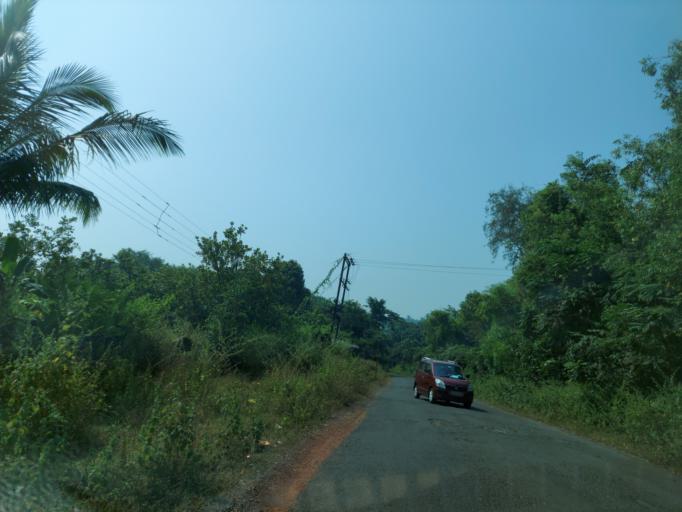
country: IN
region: Maharashtra
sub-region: Sindhudurg
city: Kudal
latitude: 15.9694
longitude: 73.6043
